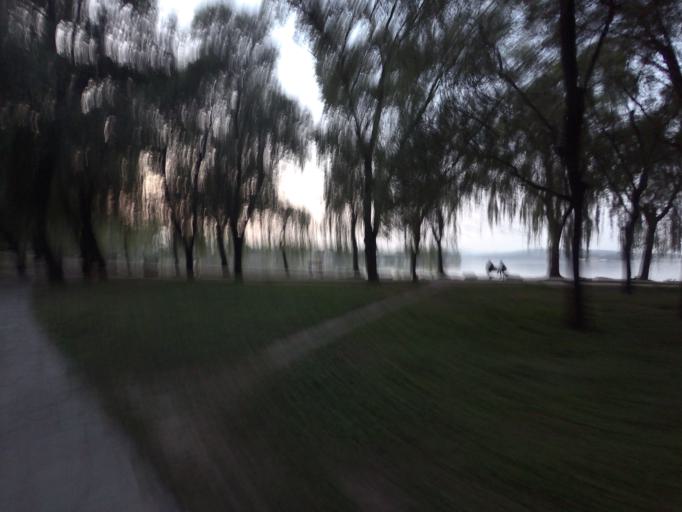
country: CN
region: Beijing
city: Haidian
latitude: 39.9813
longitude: 116.2696
